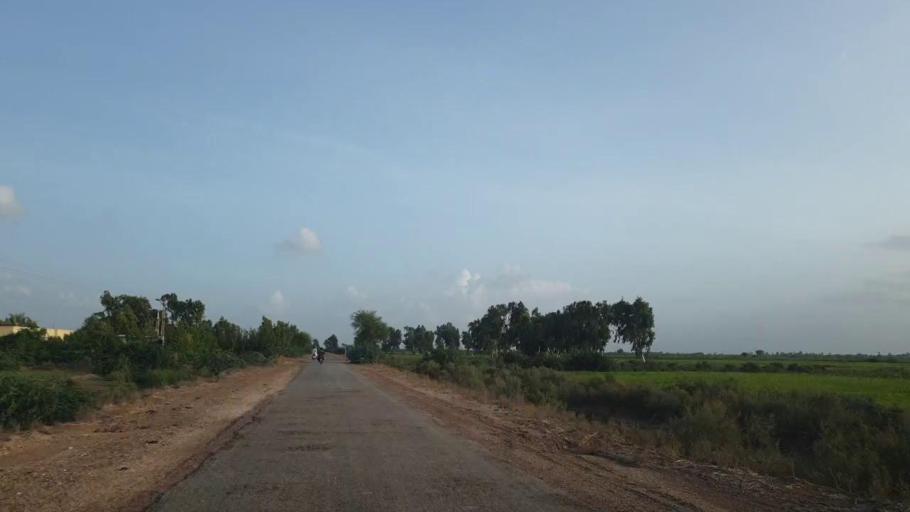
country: PK
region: Sindh
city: Kadhan
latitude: 24.6171
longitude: 69.1158
